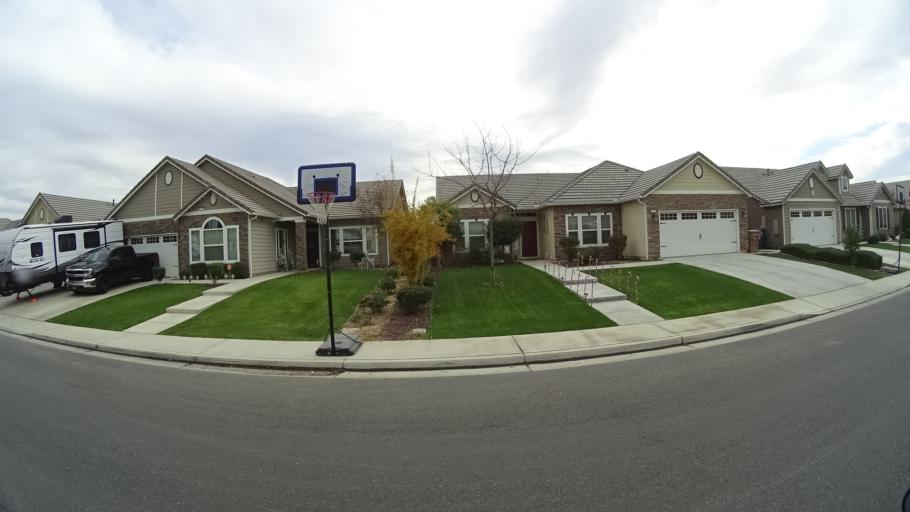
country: US
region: California
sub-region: Kern County
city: Rosedale
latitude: 35.4119
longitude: -119.1499
